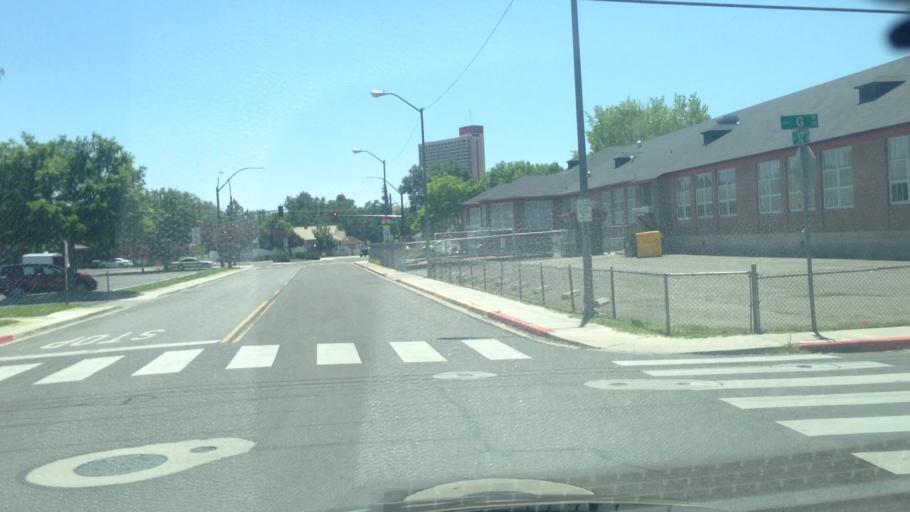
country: US
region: Nevada
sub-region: Washoe County
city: Sparks
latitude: 39.5404
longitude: -119.7584
